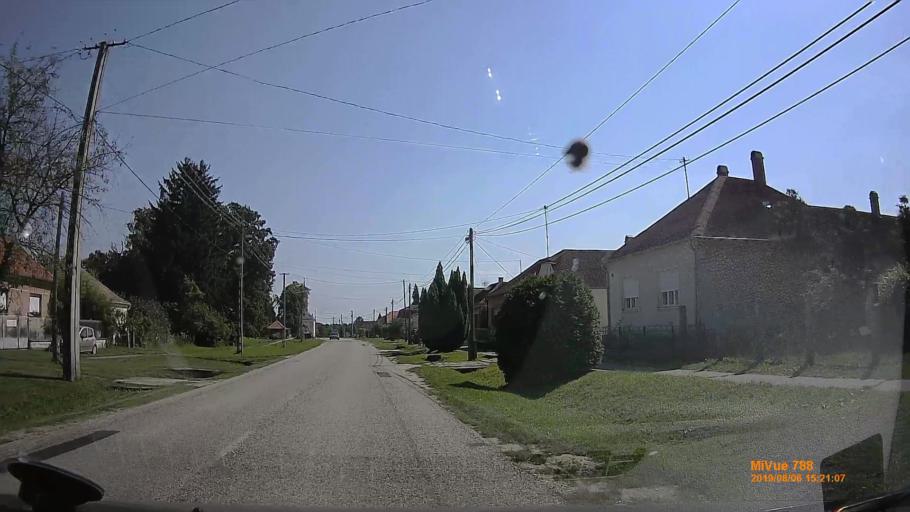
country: HR
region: Koprivnicko-Krizevacka
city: Drnje
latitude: 46.2786
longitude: 16.9471
